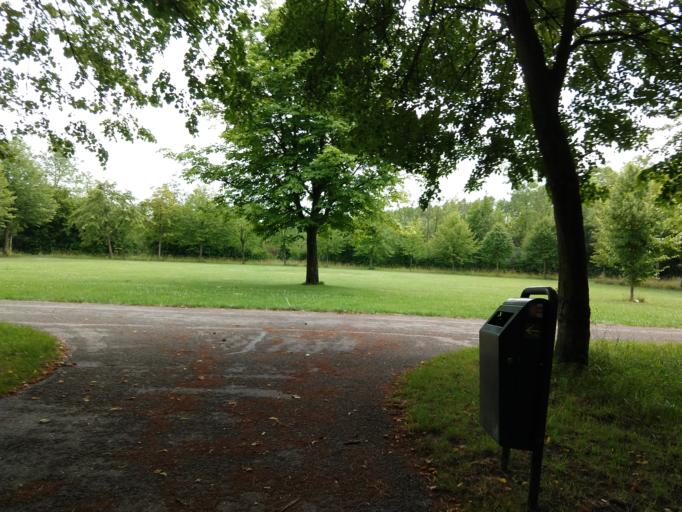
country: NL
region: Zeeland
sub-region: Gemeente Borsele
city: Borssele
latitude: 51.4696
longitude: 3.7320
